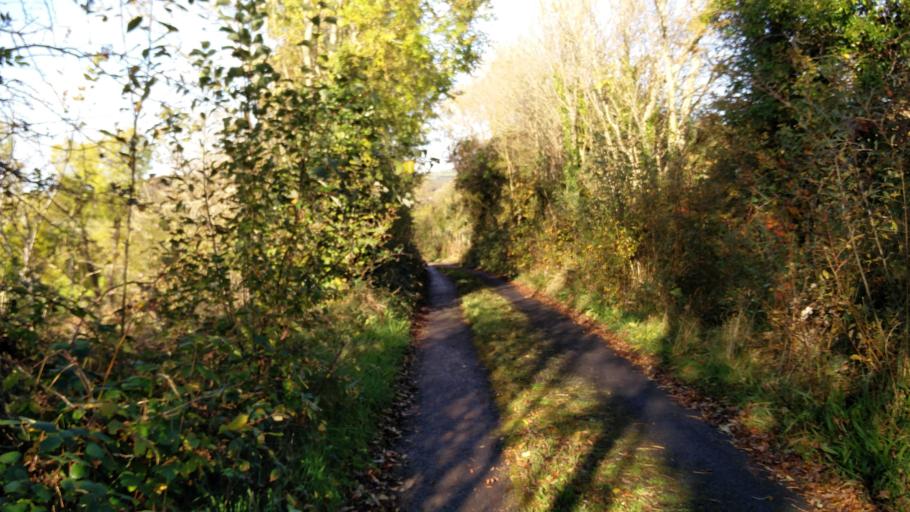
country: IE
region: Connaught
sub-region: Maigh Eo
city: Westport
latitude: 53.7825
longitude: -9.4569
